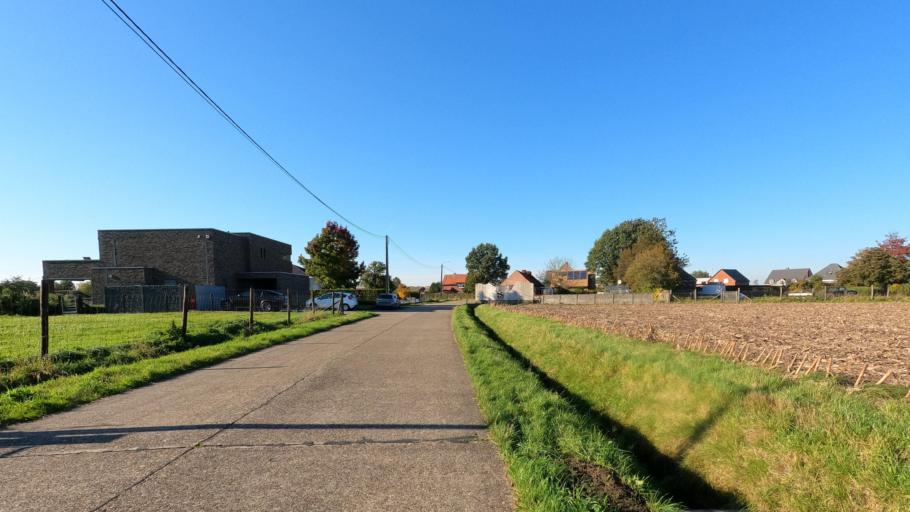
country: BE
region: Flanders
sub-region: Provincie Antwerpen
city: Herselt
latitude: 51.0869
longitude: 4.8647
